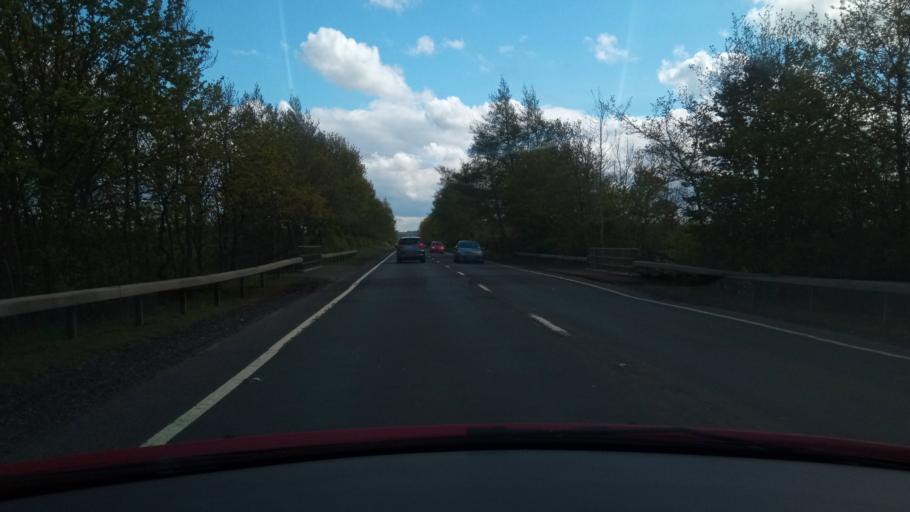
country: GB
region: Scotland
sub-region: The Scottish Borders
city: Newtown St Boswells
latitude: 55.5806
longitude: -2.6690
